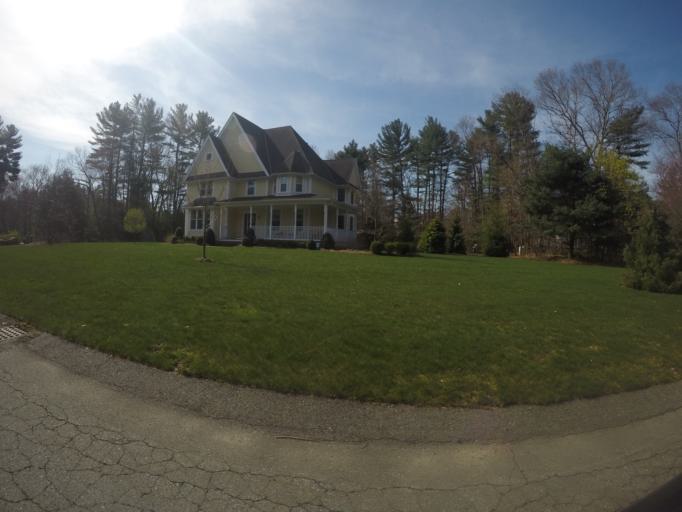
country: US
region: Massachusetts
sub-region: Bristol County
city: Easton
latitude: 42.0219
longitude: -71.1005
